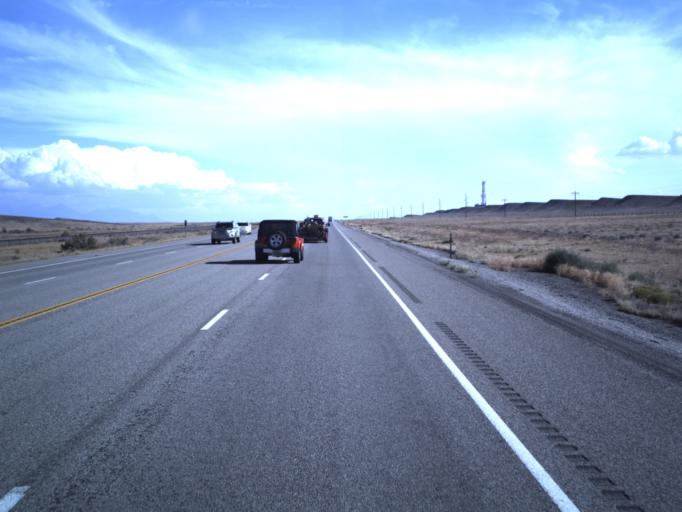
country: US
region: Utah
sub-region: Grand County
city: Moab
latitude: 38.8303
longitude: -109.7858
